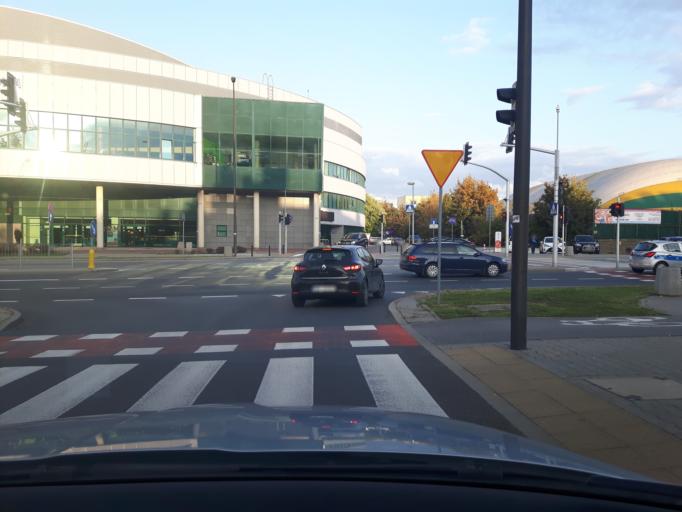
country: PL
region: Masovian Voivodeship
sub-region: Warszawa
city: Ursynow
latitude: 52.1428
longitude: 21.0383
